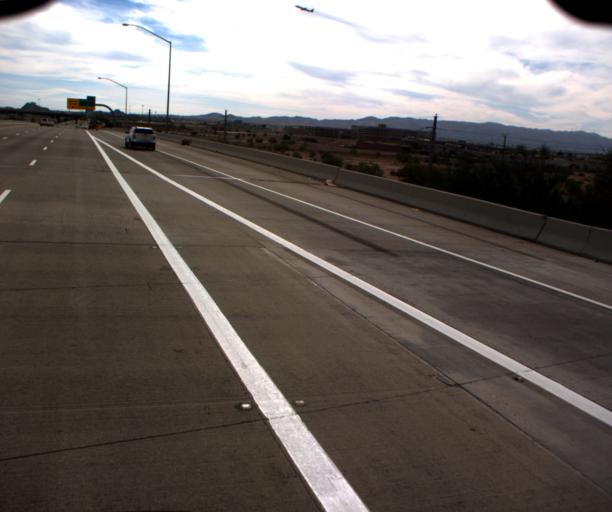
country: US
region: Arizona
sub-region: Maricopa County
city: Tempe Junction
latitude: 33.4443
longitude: -111.9810
